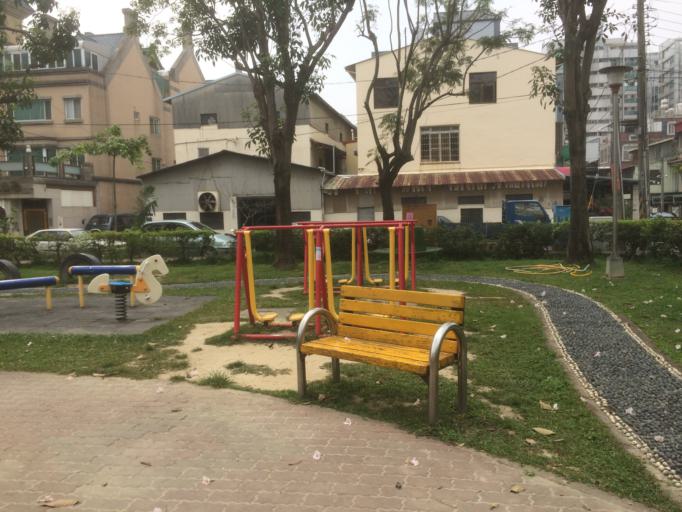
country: TW
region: Taiwan
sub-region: Taichung City
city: Taichung
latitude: 24.1858
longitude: 120.7015
